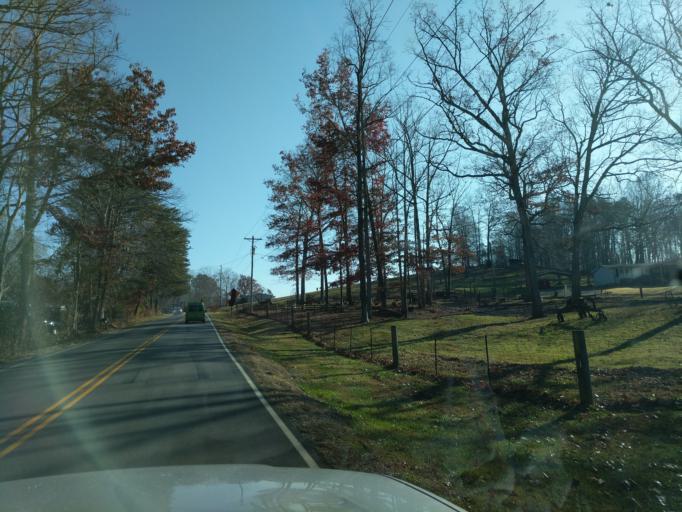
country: US
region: North Carolina
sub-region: Rutherford County
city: Rutherfordton
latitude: 35.2718
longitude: -82.0386
